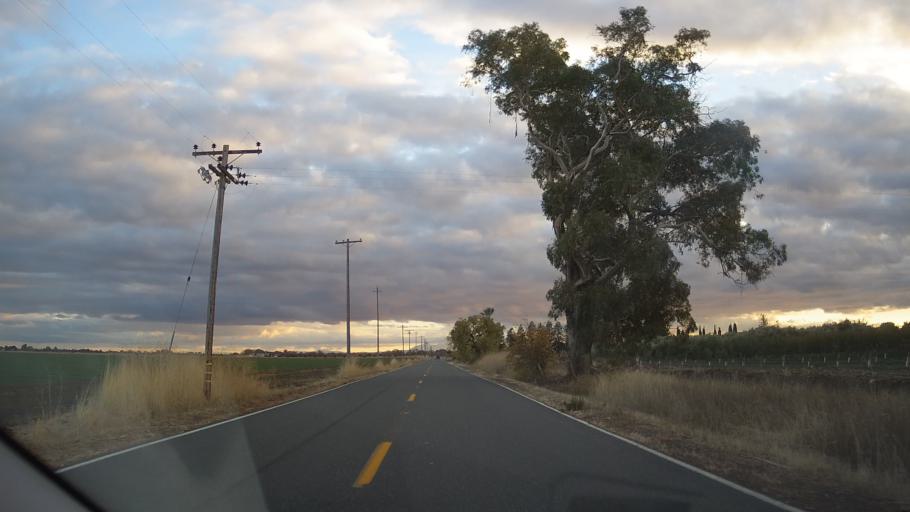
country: US
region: California
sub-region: Solano County
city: Hartley
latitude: 38.3791
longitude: -121.9059
